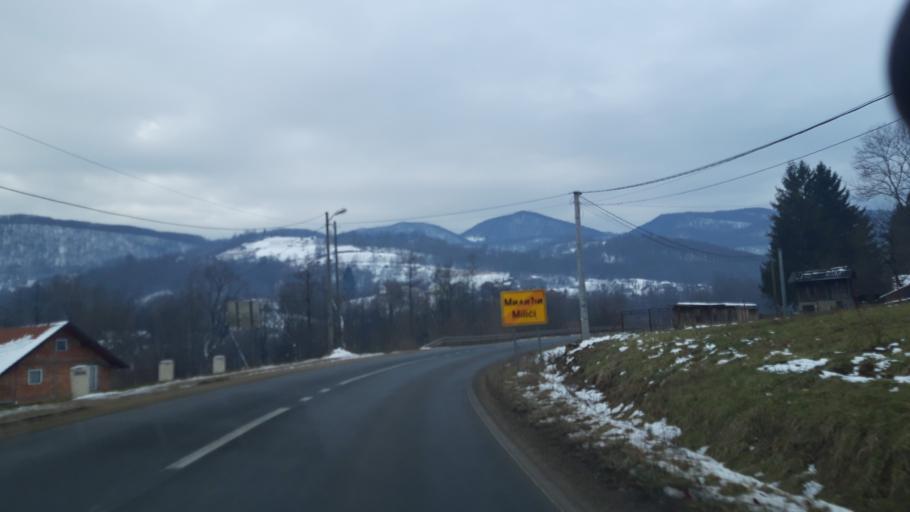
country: BA
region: Republika Srpska
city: Milici
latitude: 44.1640
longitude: 19.0671
